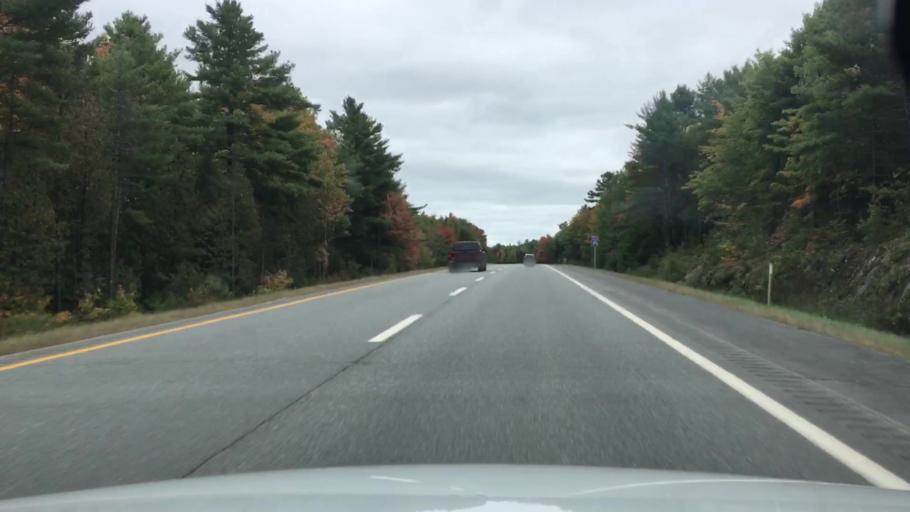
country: US
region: Maine
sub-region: Penobscot County
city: Plymouth
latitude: 44.7969
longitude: -69.2129
